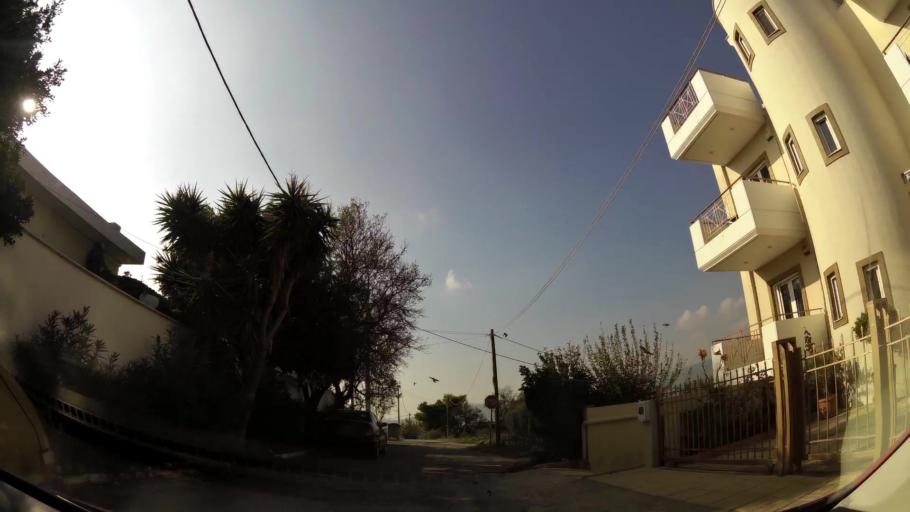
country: GR
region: Attica
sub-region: Nomarchia Dytikis Attikis
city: Zefyri
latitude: 38.0704
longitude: 23.7289
